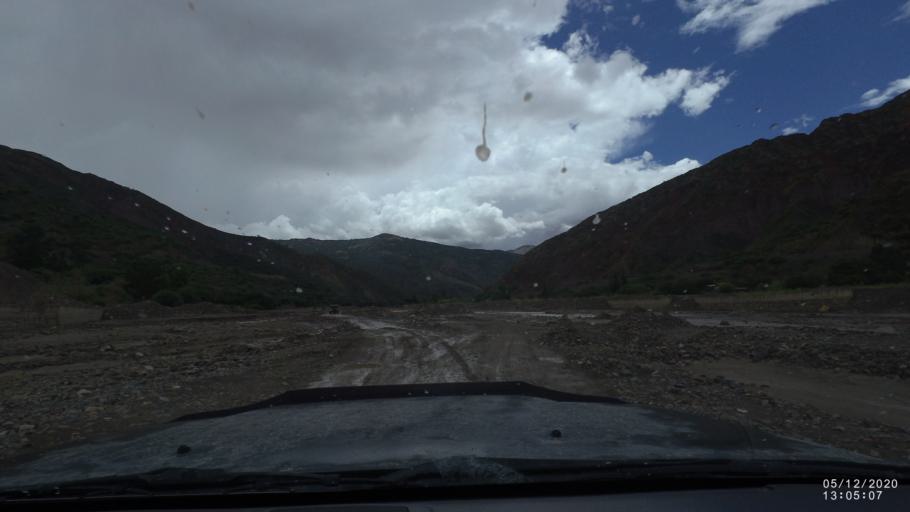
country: BO
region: Cochabamba
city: Sipe Sipe
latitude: -17.5535
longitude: -66.4417
